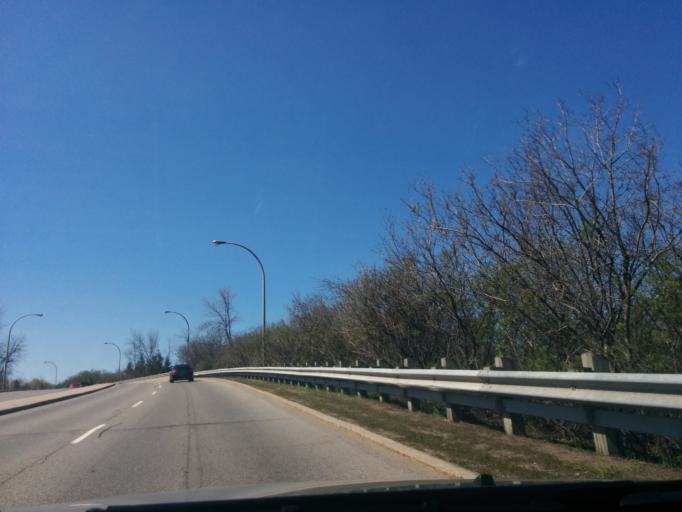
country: CA
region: Ontario
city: Ottawa
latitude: 45.3803
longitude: -75.6906
